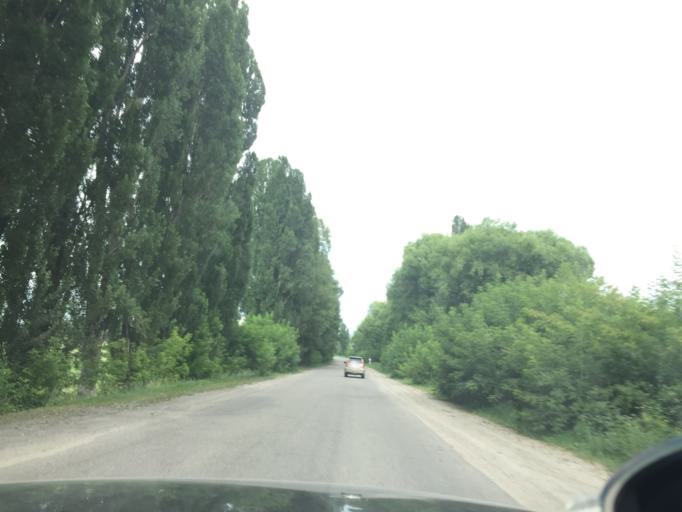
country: KG
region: Ysyk-Koel
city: Teploklyuchenka
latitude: 42.5204
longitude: 78.6139
